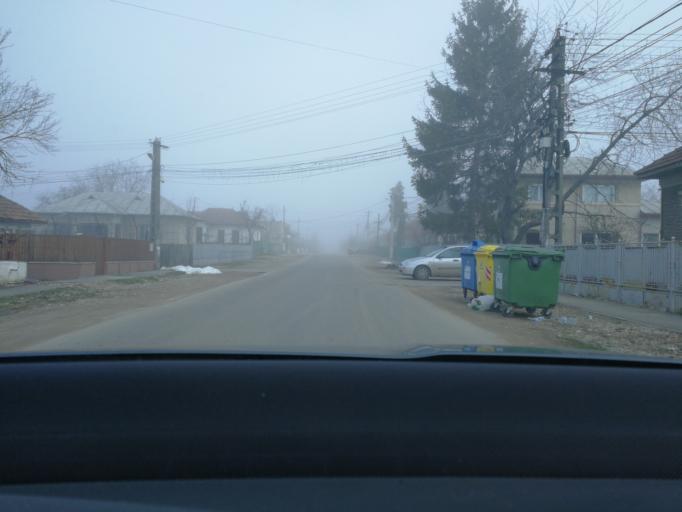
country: RO
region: Prahova
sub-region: Comuna Magureni
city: Lunca Prahovei
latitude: 45.0460
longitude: 25.7504
